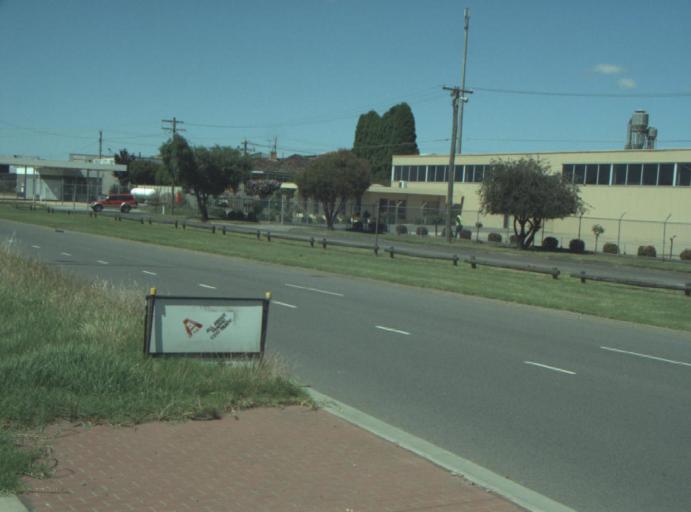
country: AU
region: Victoria
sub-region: Greater Geelong
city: Breakwater
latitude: -38.1818
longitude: 144.3542
